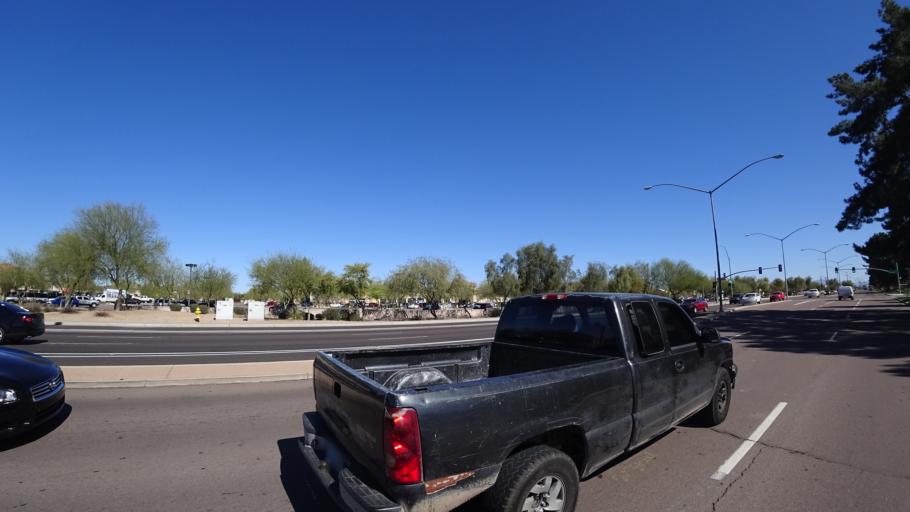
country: US
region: Arizona
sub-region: Maricopa County
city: San Carlos
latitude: 33.3787
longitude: -111.8384
